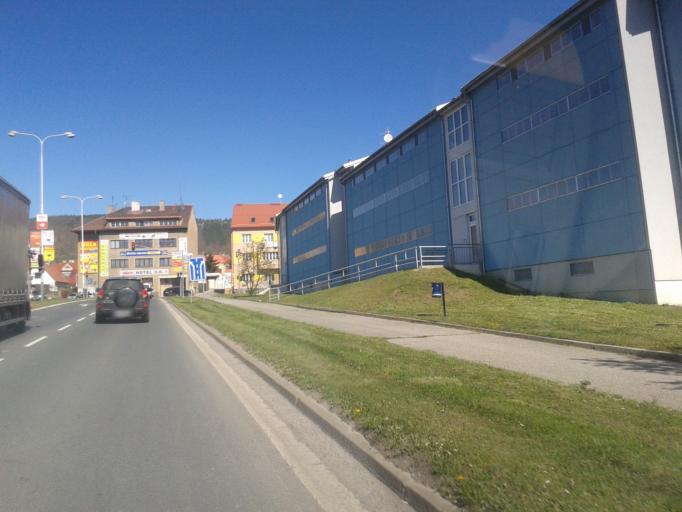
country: CZ
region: Central Bohemia
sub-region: Okres Beroun
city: Beroun
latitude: 49.9581
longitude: 14.0626
